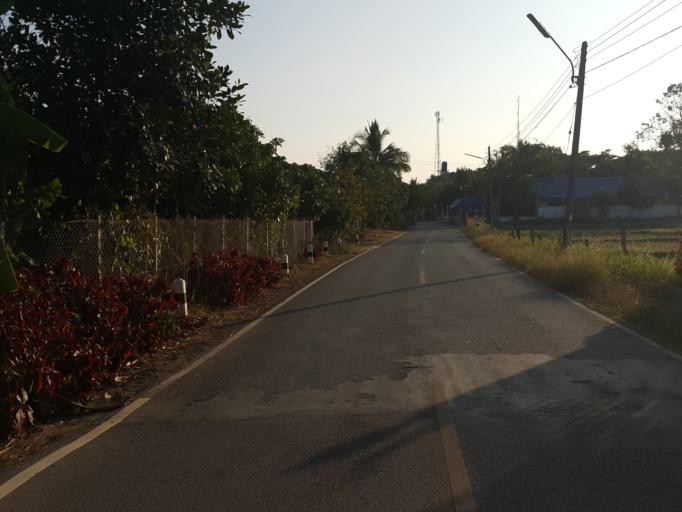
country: TH
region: Chiang Mai
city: Mae On
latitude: 18.7895
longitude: 99.2541
